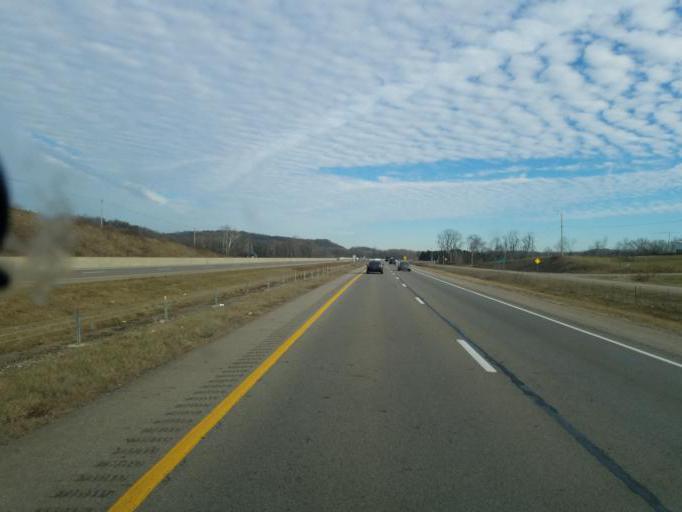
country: US
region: Ohio
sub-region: Licking County
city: Granville South
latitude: 40.0704
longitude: -82.5675
